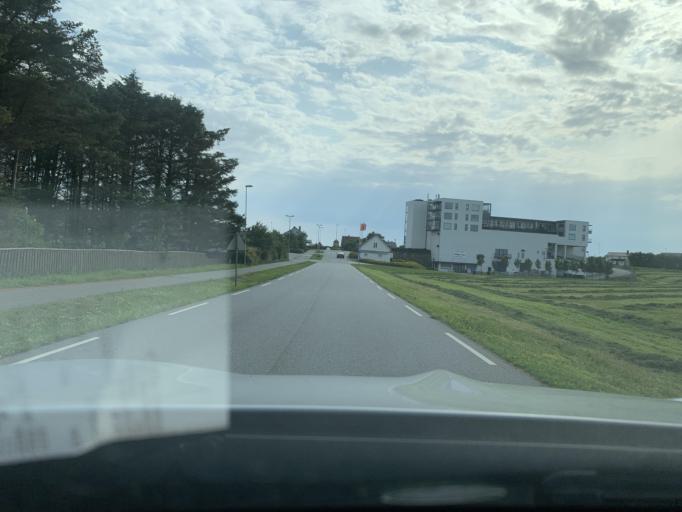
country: NO
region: Rogaland
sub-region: Time
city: Bryne
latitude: 58.7195
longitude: 5.5710
